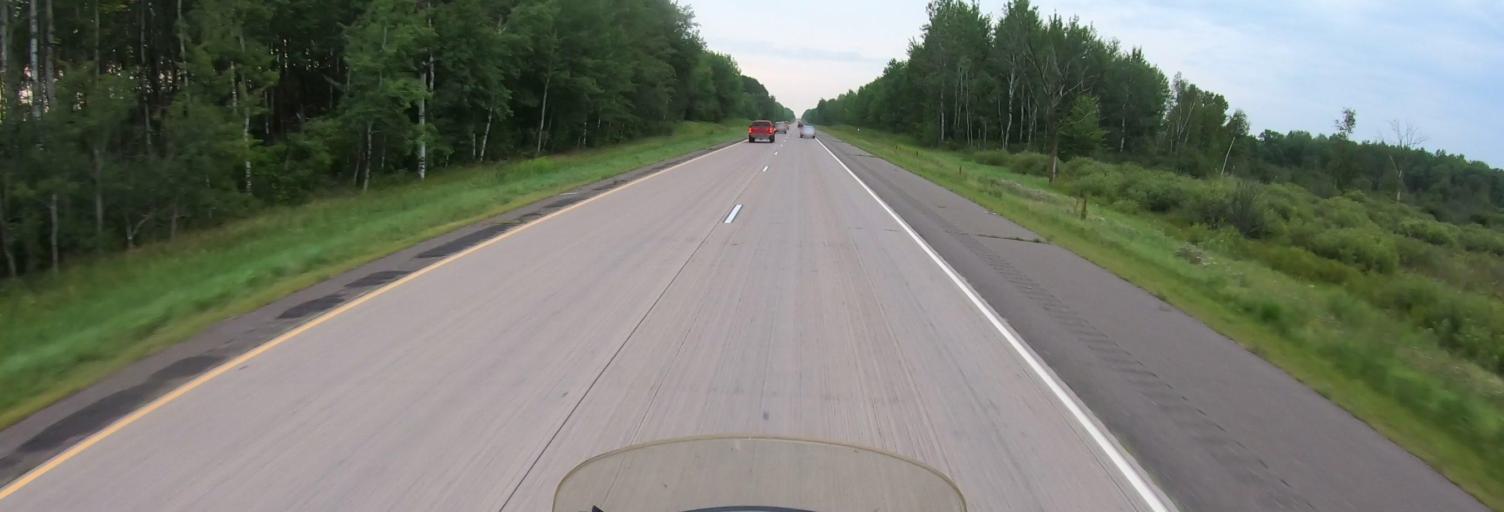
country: US
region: Minnesota
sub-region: Pine County
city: Hinckley
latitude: 46.0557
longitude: -92.9112
